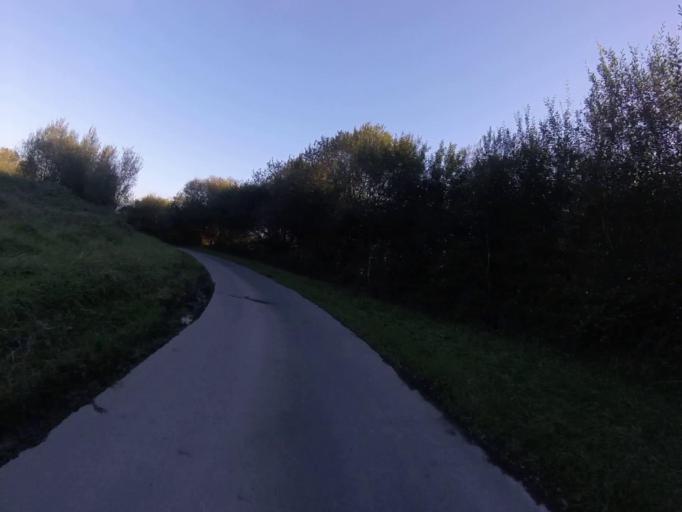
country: ES
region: Basque Country
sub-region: Provincia de Guipuzcoa
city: Lasarte
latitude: 43.2821
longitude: -2.0097
